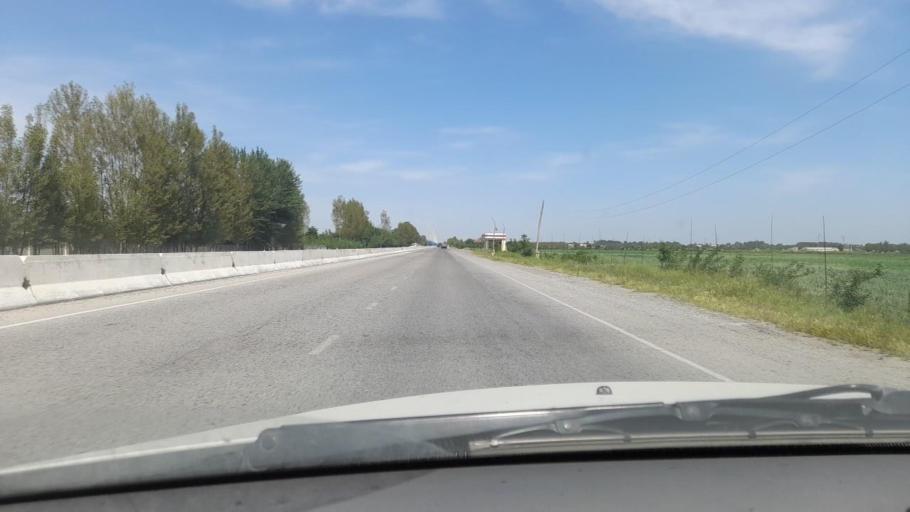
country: UZ
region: Samarqand
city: Ishtixon
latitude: 39.9349
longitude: 66.3737
